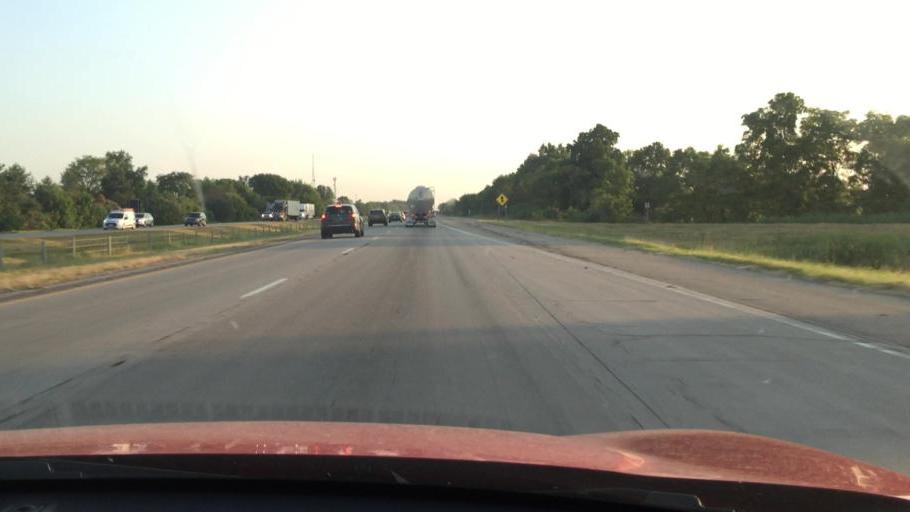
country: US
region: Michigan
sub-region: Washtenaw County
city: Milan
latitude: 42.1588
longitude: -83.6839
